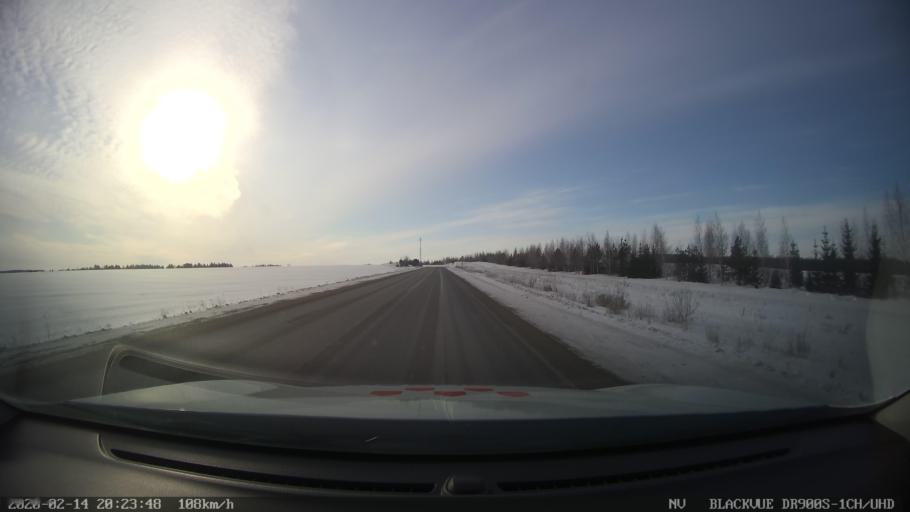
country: RU
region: Tatarstan
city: Verkhniy Uslon
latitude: 55.5223
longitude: 48.9676
